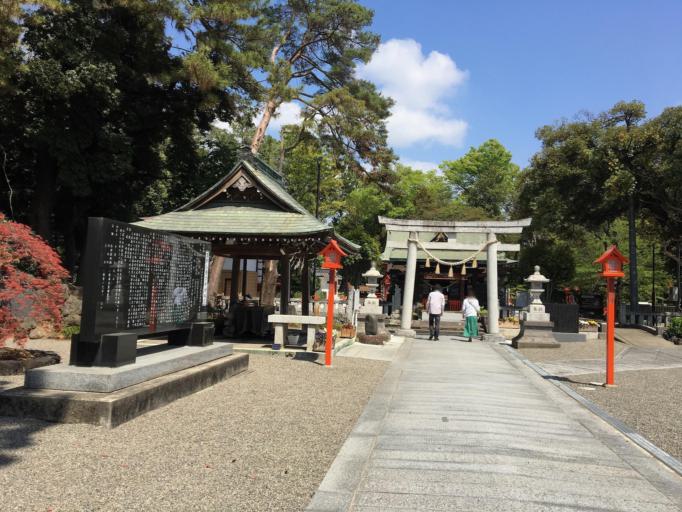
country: JP
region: Gunma
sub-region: Sawa-gun
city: Tamamura
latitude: 36.3046
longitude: 139.1087
